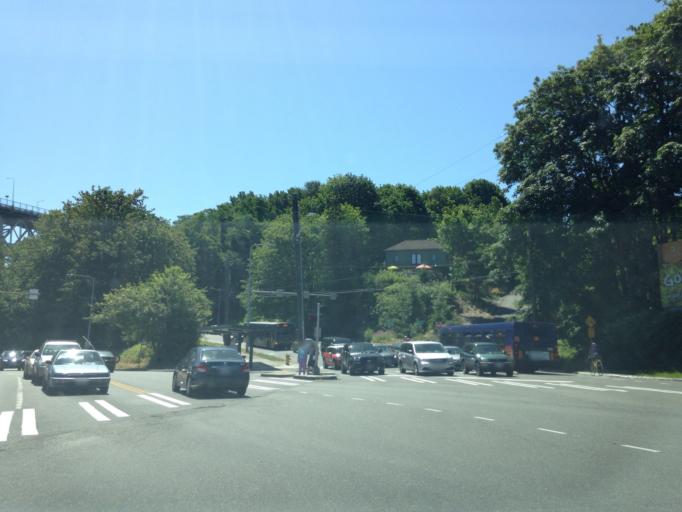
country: US
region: Washington
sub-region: King County
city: Seattle
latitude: 47.6462
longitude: -122.3497
